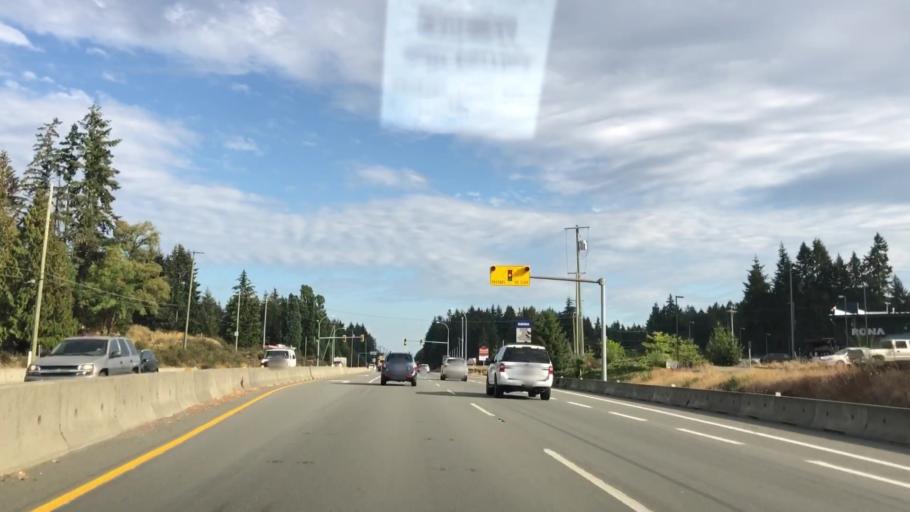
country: CA
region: British Columbia
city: Duncan
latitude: 48.6969
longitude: -123.5929
